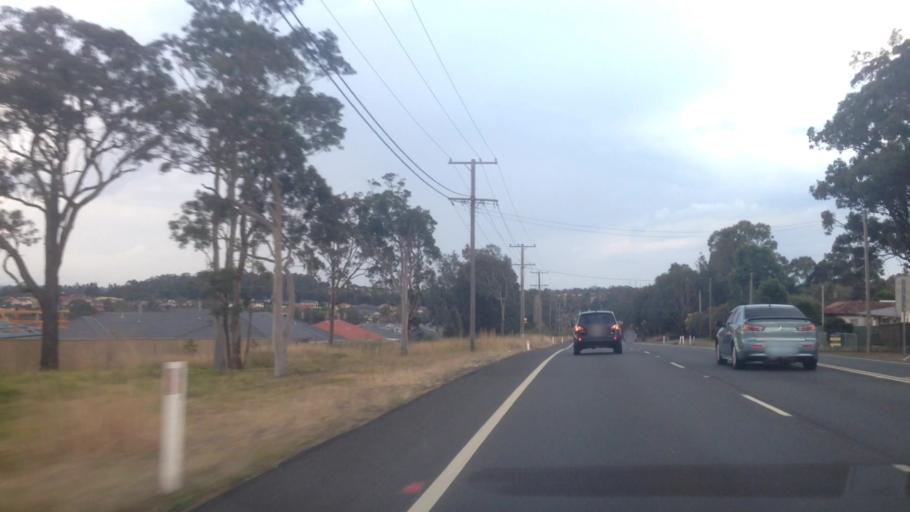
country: AU
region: New South Wales
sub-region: Wyong Shire
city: Kanwal
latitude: -33.2590
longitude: 151.4852
